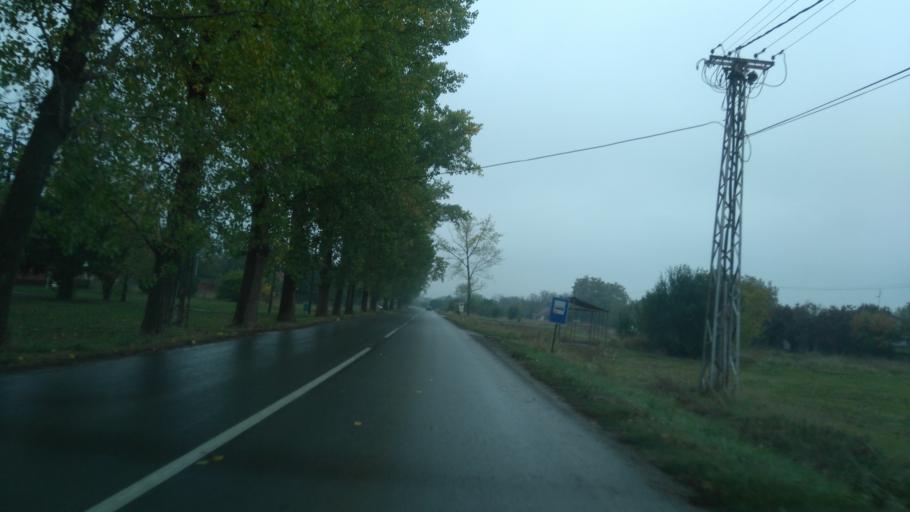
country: RS
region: Autonomna Pokrajina Vojvodina
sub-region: Juznobacki Okrug
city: Becej
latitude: 45.6384
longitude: 20.0285
